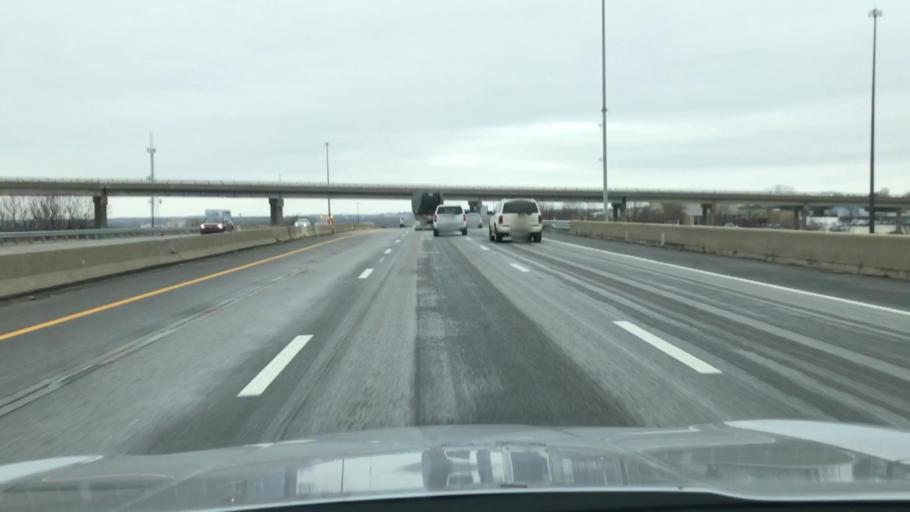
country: US
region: Missouri
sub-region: Saint Louis County
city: Bridgeton
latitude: 38.7486
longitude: -90.4396
